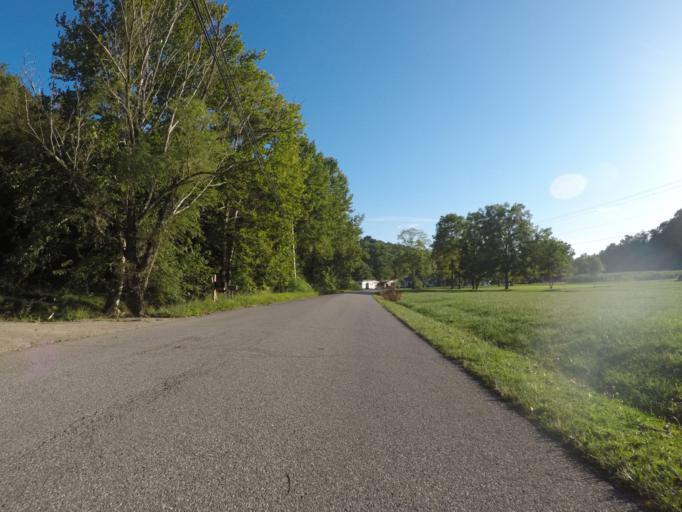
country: US
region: Ohio
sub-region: Lawrence County
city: Coal Grove
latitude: 38.5378
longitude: -82.5404
